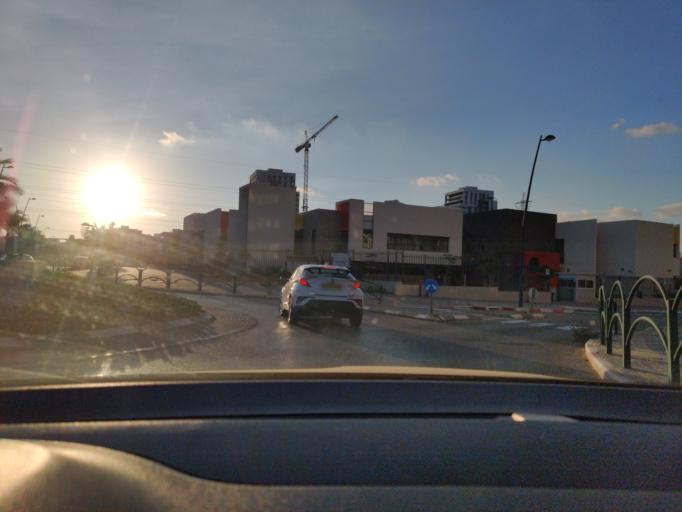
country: IL
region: Central District
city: Elyakhin
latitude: 32.4273
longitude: 34.9359
